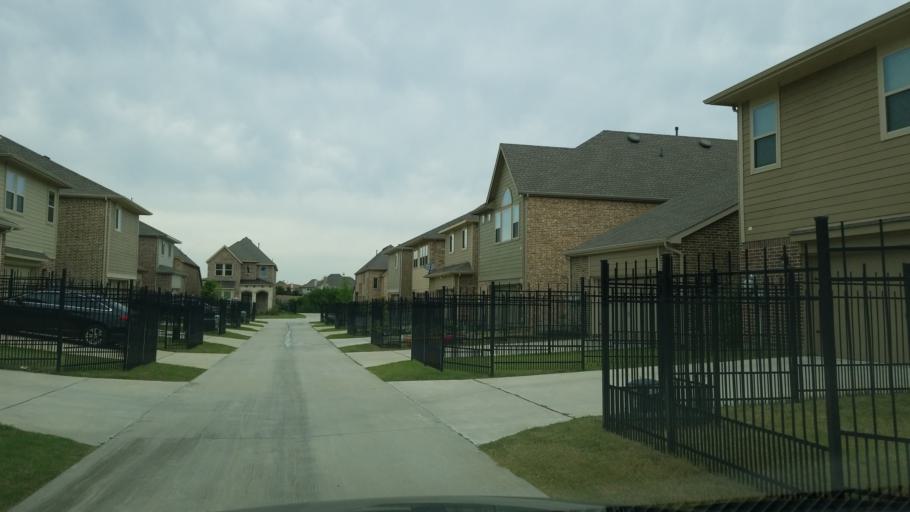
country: US
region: Texas
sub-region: Dallas County
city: Coppell
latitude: 32.9003
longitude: -96.9857
